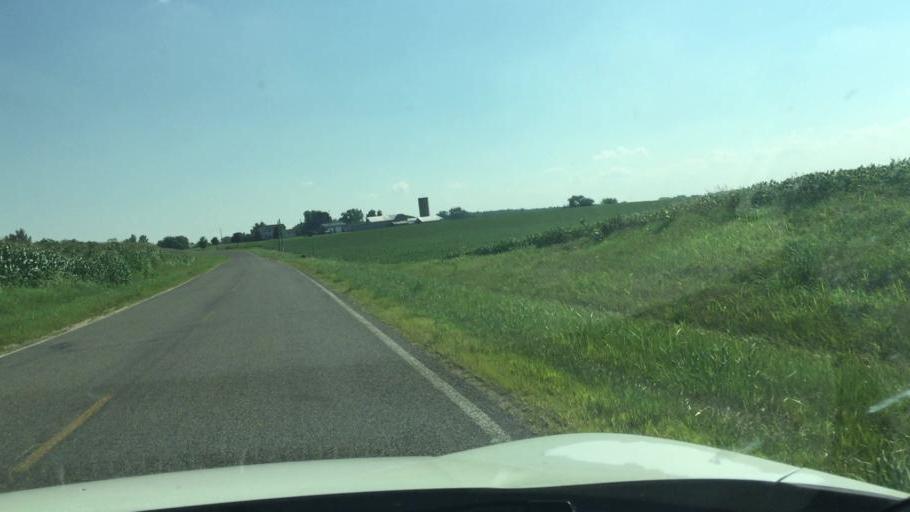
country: US
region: Ohio
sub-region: Champaign County
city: Mechanicsburg
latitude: 40.0619
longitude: -83.6534
